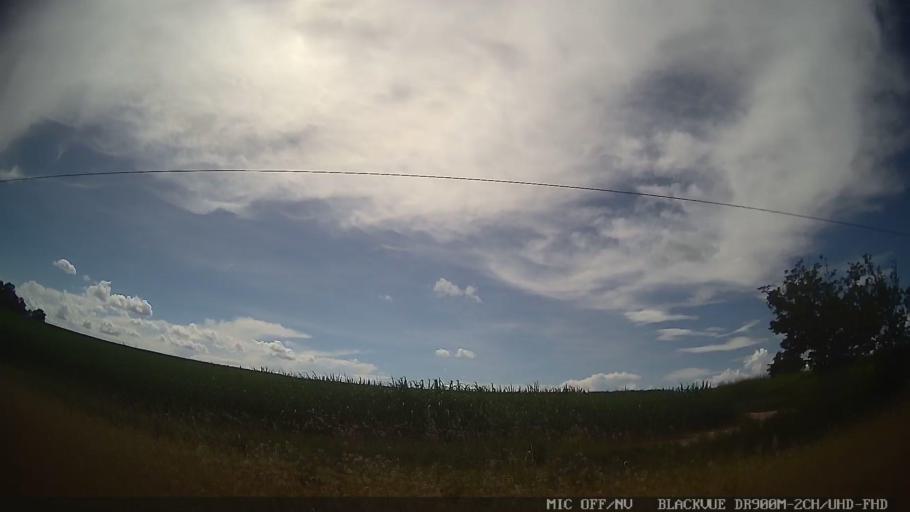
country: BR
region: Sao Paulo
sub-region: Conchas
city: Conchas
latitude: -22.9752
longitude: -47.9874
